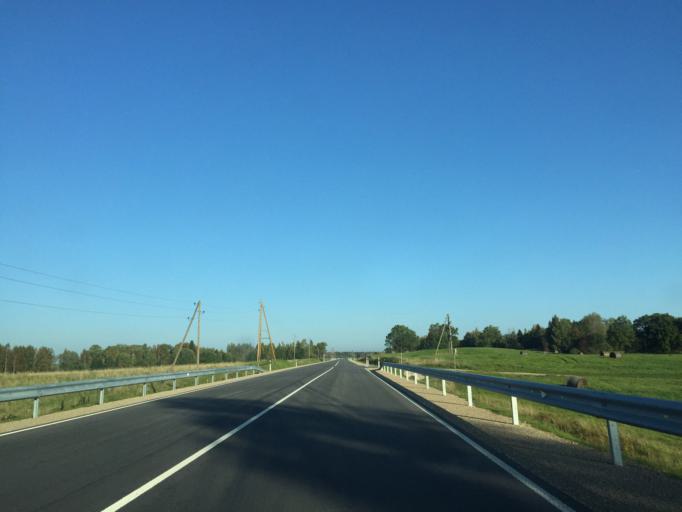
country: LV
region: Vecpiebalga
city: Vecpiebalga
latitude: 57.0882
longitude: 25.7407
